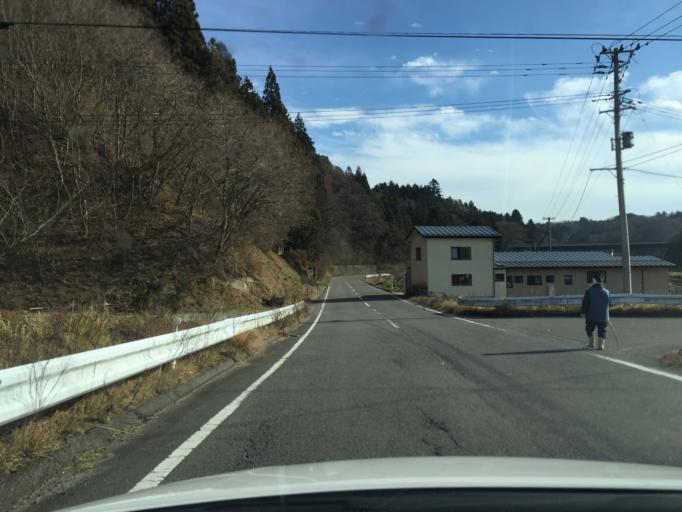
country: JP
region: Fukushima
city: Funehikimachi-funehiki
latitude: 37.2781
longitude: 140.5915
